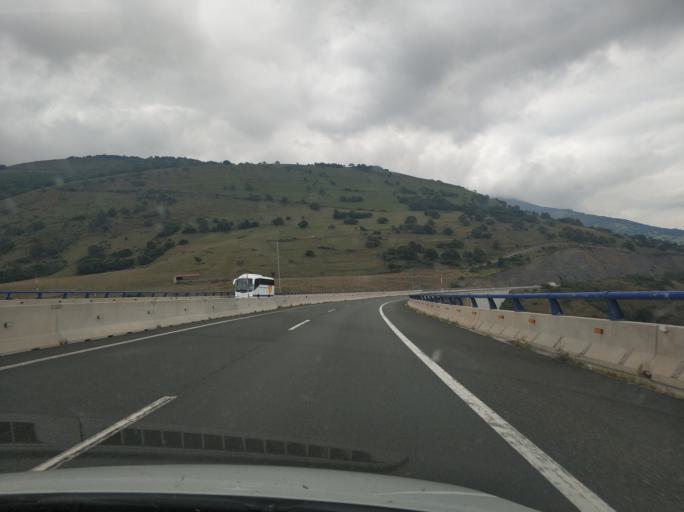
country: ES
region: Cantabria
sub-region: Provincia de Cantabria
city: Pesquera
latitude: 43.1039
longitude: -4.0902
